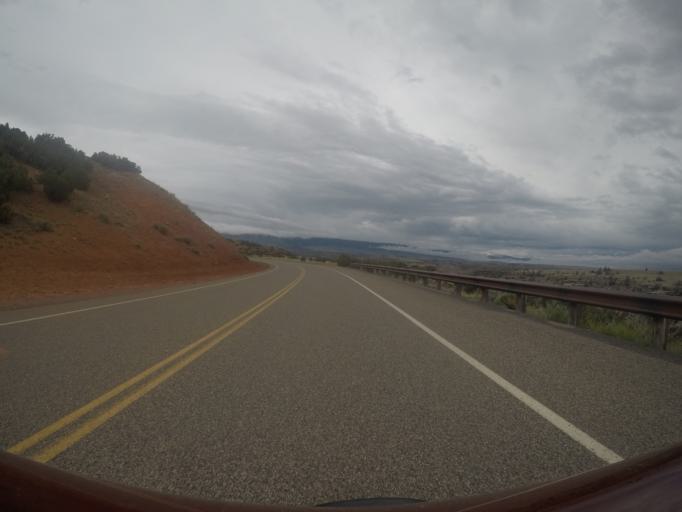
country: US
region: Wyoming
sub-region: Big Horn County
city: Lovell
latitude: 45.1017
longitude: -108.2400
